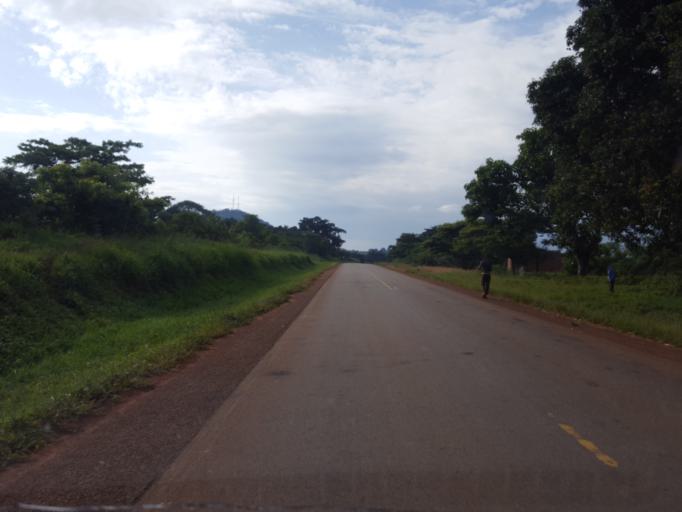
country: UG
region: Western Region
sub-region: Hoima District
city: Hoima
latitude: 1.2659
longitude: 31.4998
